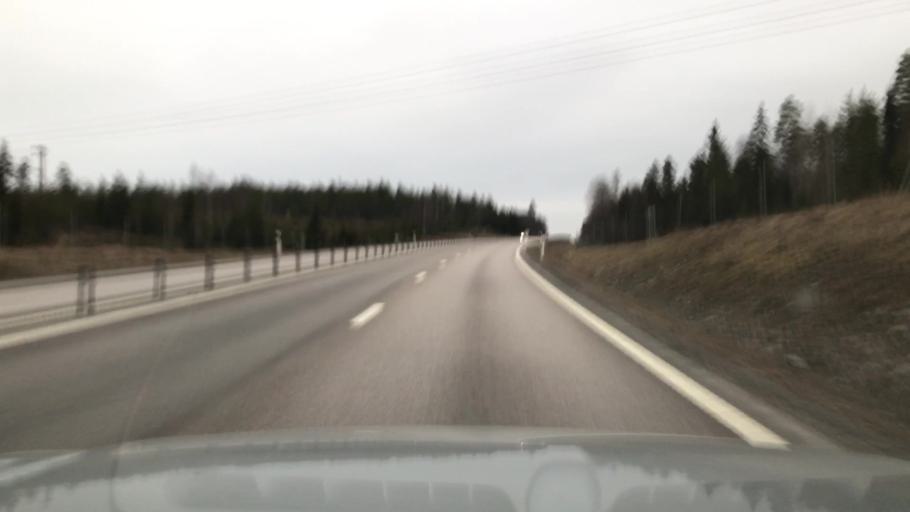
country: SE
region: OEstergoetland
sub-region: Valdemarsviks Kommun
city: Gusum
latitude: 58.2912
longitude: 16.4960
